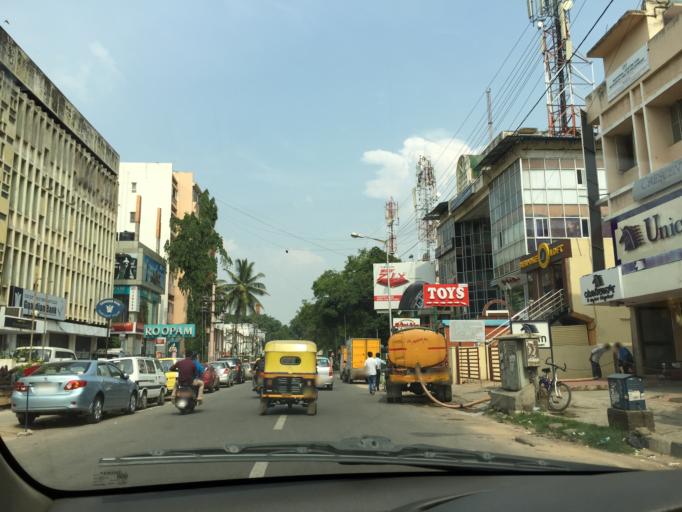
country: IN
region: Karnataka
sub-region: Bangalore Urban
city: Bangalore
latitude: 12.9798
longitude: 77.6055
